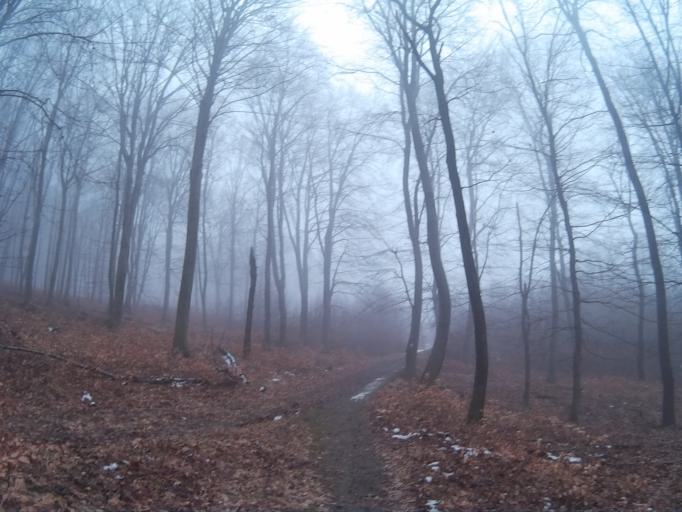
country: HU
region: Komarom-Esztergom
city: Tardos
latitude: 47.6788
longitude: 18.4710
